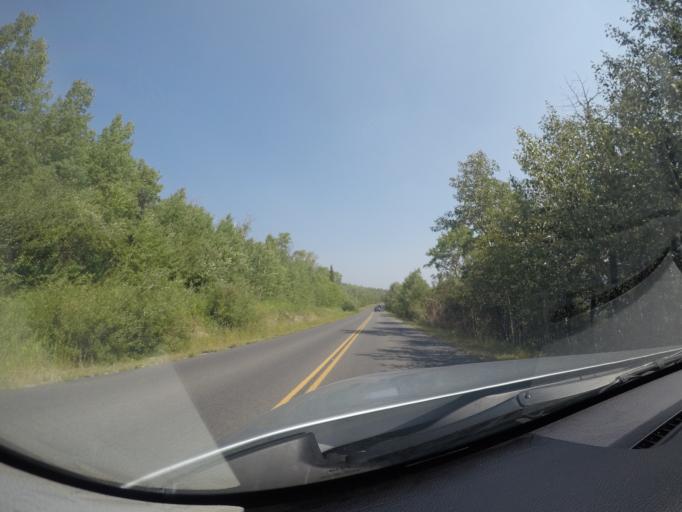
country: US
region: Montana
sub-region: Glacier County
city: North Browning
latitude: 48.7352
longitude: -113.4602
